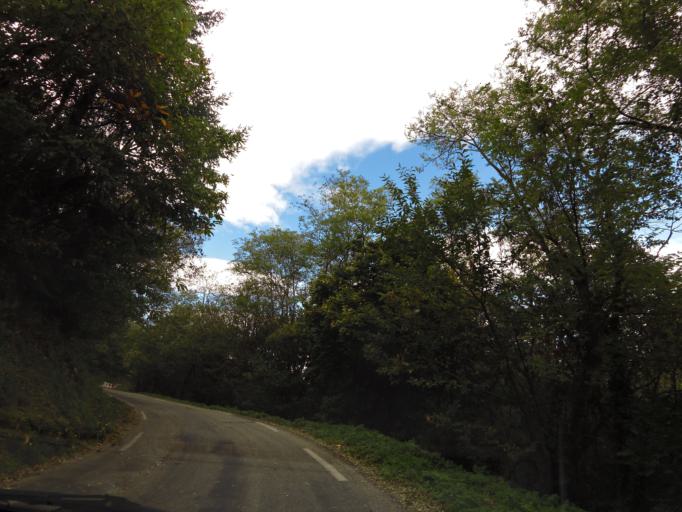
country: FR
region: Languedoc-Roussillon
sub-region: Departement du Gard
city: Lasalle
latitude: 44.0223
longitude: 3.8571
